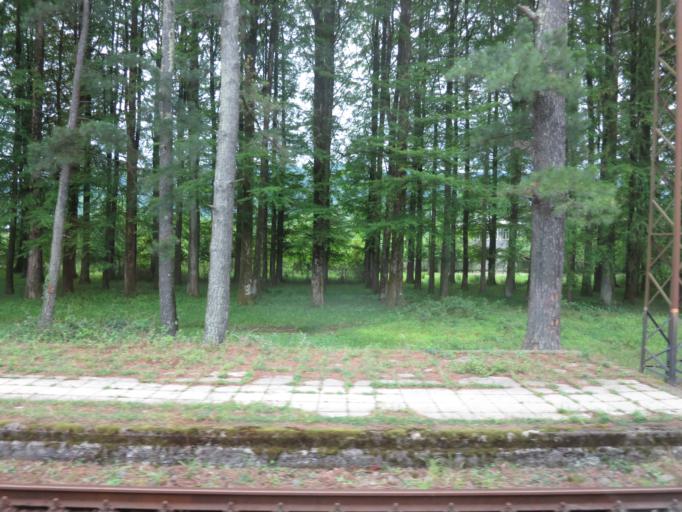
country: GE
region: Guria
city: Lanchkhuti
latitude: 42.0889
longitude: 42.1207
